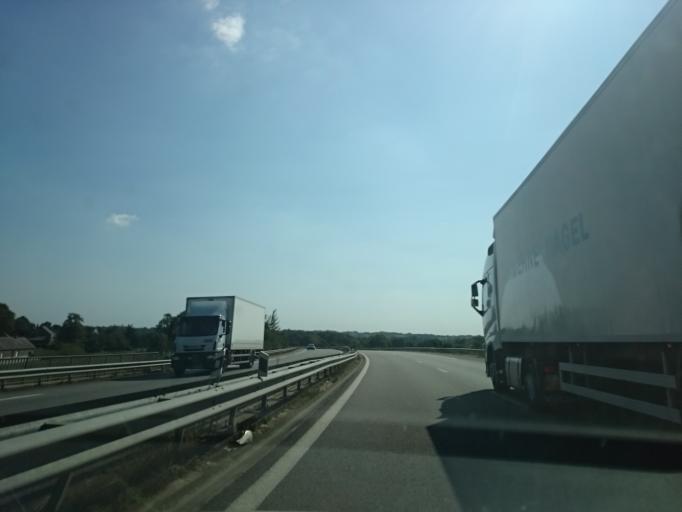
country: FR
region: Brittany
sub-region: Departement d'Ille-et-Vilaine
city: La Dominelais
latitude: 47.7824
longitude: -1.6991
